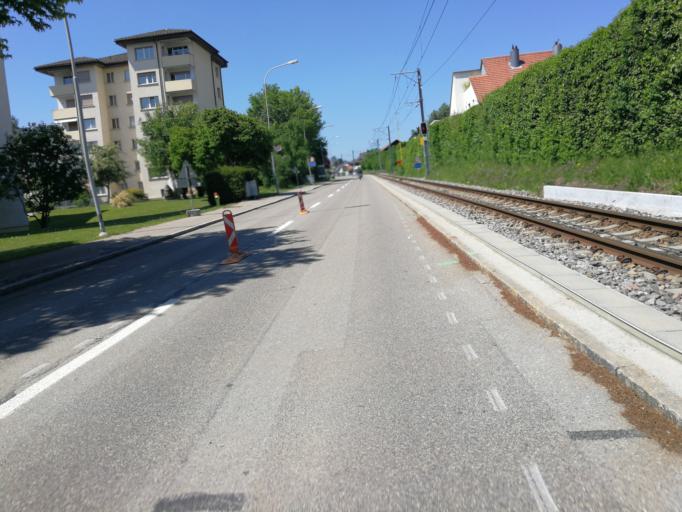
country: CH
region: Zurich
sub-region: Bezirk Uster
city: Hinteregg
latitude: 47.3040
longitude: 8.6870
